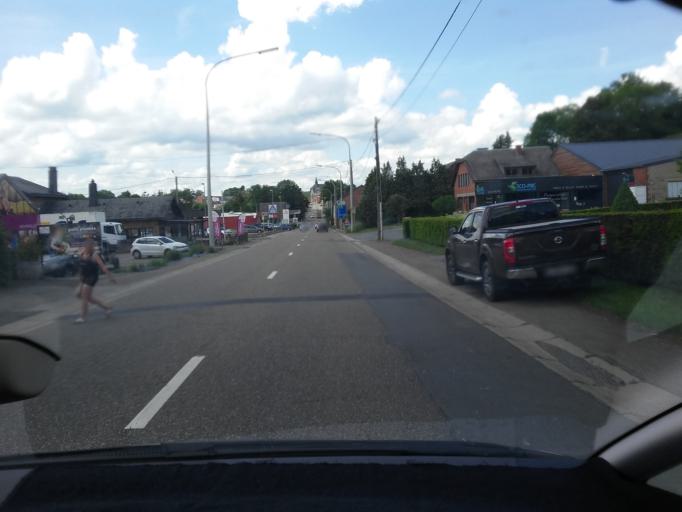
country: BE
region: Wallonia
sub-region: Province de Namur
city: Rochefort
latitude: 50.1640
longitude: 5.2154
